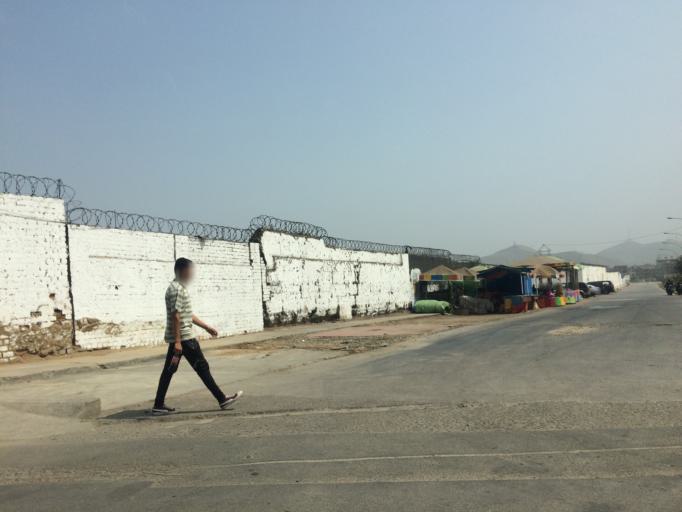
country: PE
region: Lima
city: Lima
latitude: -12.0326
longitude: -77.0379
